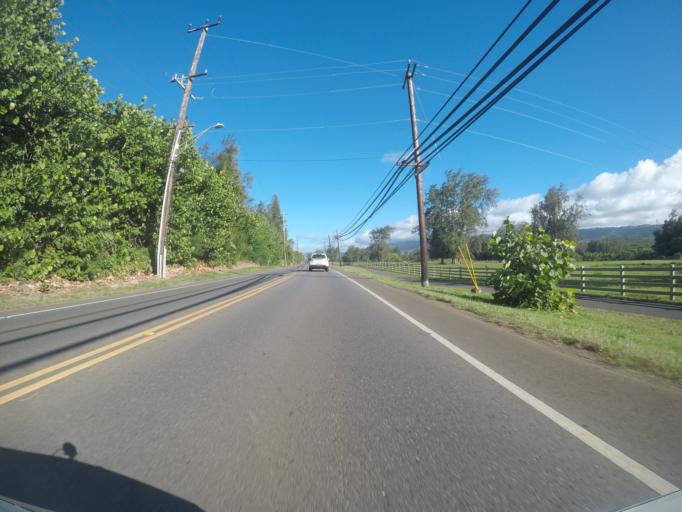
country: US
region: Hawaii
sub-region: Honolulu County
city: Kahuku
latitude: 21.6674
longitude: -157.9380
